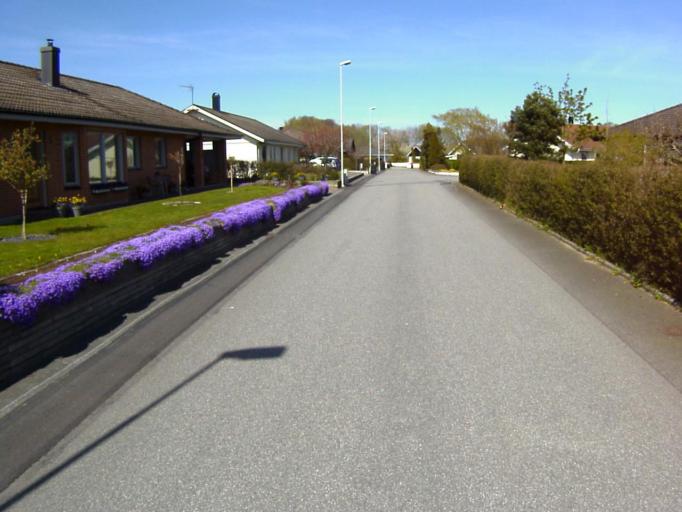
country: SE
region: Skane
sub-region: Kristianstads Kommun
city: Onnestad
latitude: 55.9988
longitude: 14.0691
